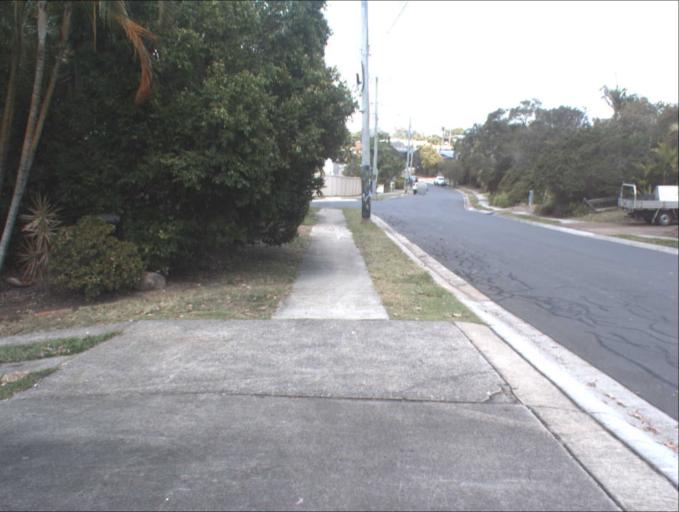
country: AU
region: Queensland
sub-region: Logan
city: Slacks Creek
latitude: -27.6383
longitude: 153.1637
